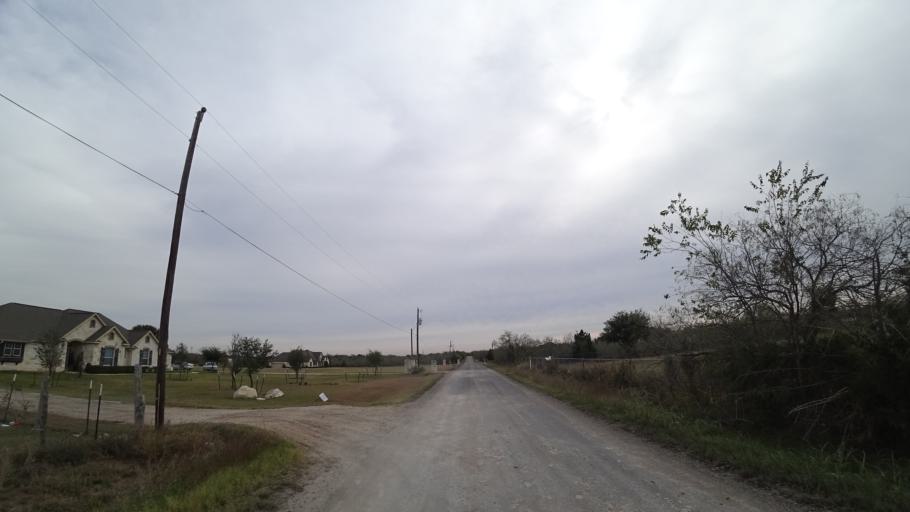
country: US
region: Texas
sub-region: Travis County
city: Garfield
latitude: 30.1127
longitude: -97.5791
